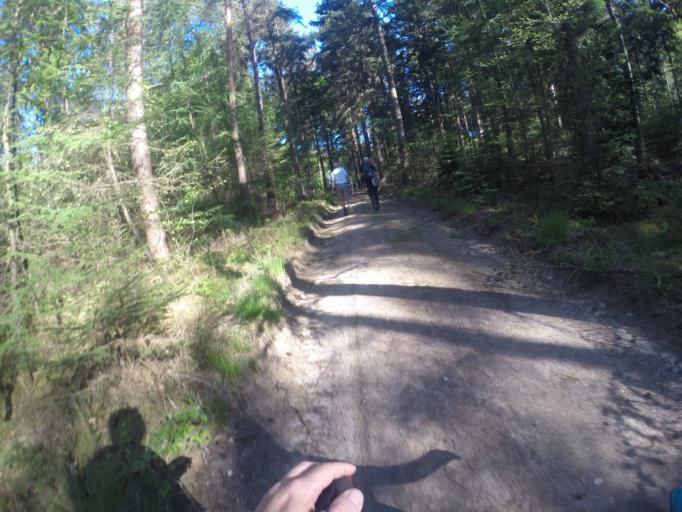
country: NL
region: Gelderland
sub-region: Gemeente Montferland
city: s-Heerenberg
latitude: 51.9039
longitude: 6.2281
